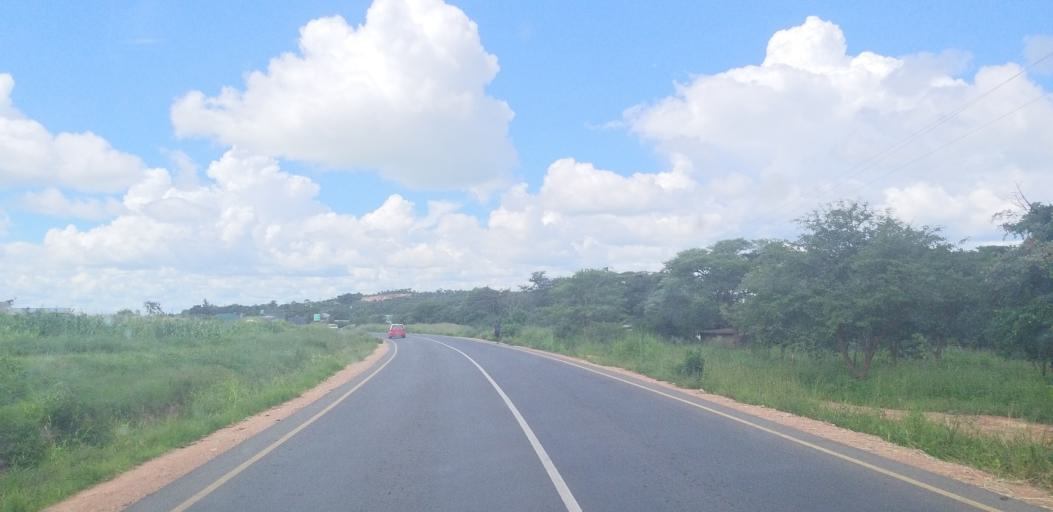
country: ZM
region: Lusaka
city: Lusaka
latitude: -15.3318
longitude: 28.3287
